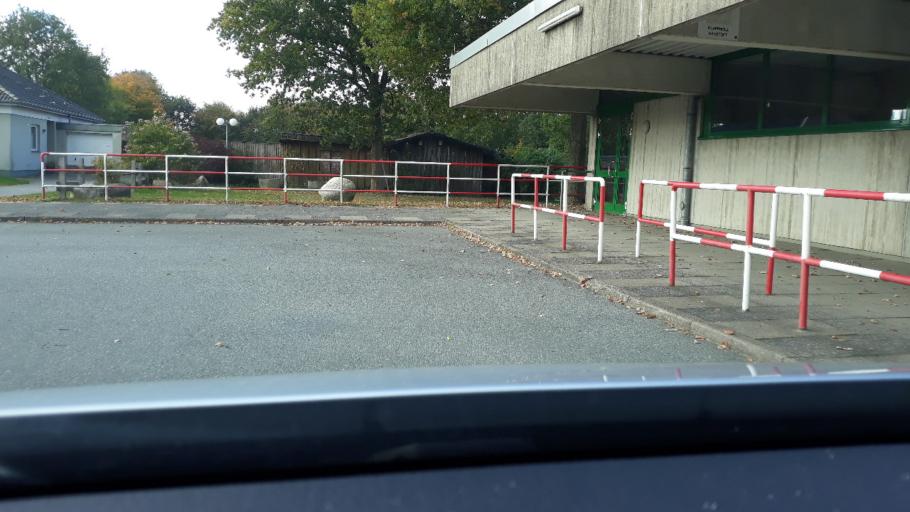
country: DE
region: Schleswig-Holstein
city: Boklund
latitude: 54.6032
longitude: 9.5745
